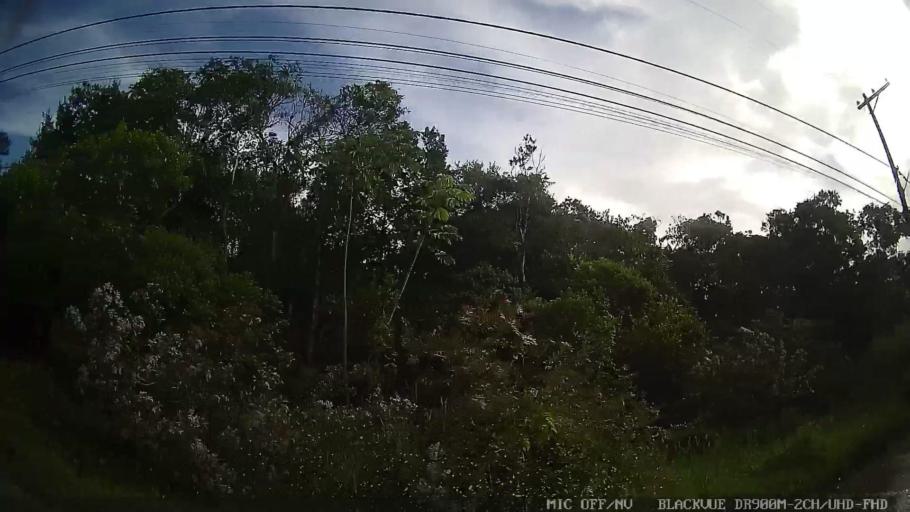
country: BR
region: Sao Paulo
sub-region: Itanhaem
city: Itanhaem
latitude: -24.2128
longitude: -46.8740
